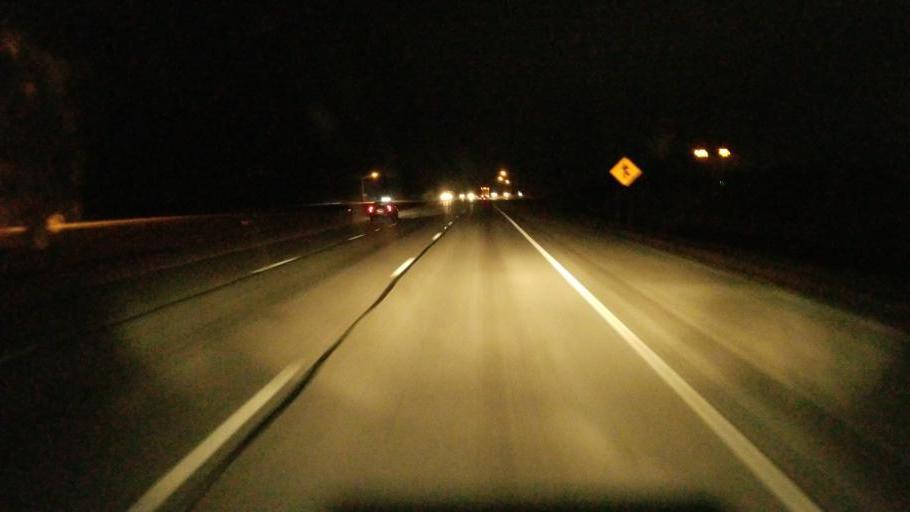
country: US
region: Ohio
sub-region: Clark County
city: Lisbon
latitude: 39.9221
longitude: -83.6900
